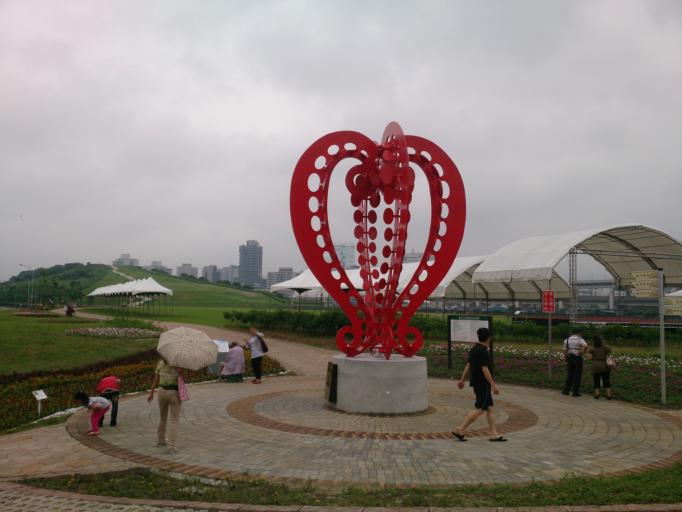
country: TW
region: Taipei
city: Taipei
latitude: 25.0609
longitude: 121.6030
